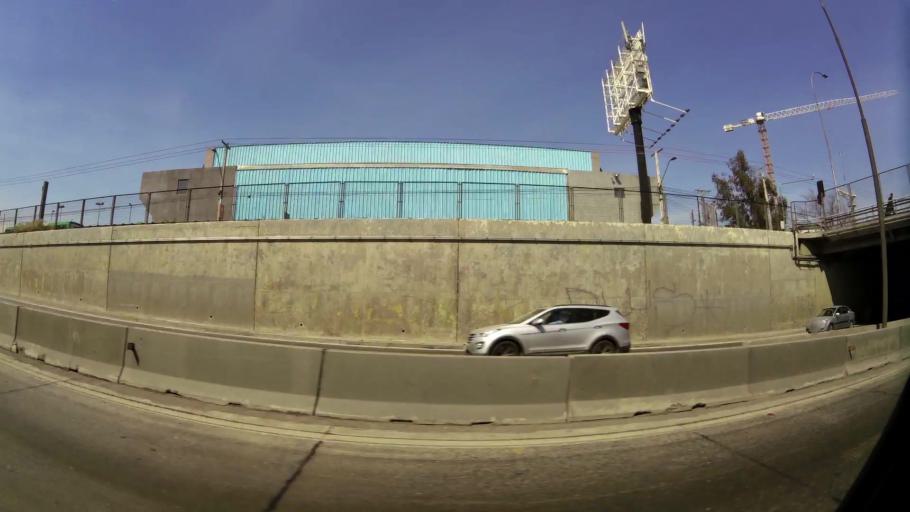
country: CL
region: Santiago Metropolitan
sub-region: Provincia de Santiago
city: Santiago
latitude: -33.4898
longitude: -70.6612
